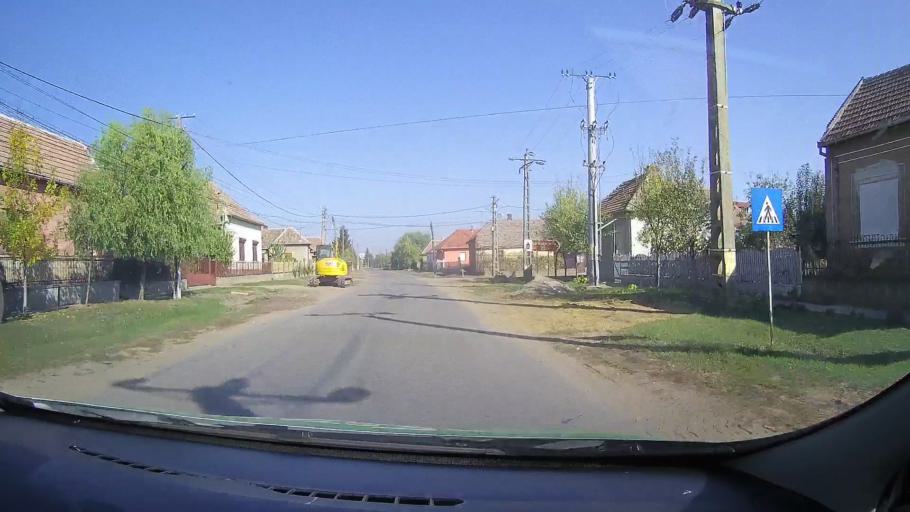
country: RO
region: Satu Mare
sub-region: Comuna Ciumesti
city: Ciumesti
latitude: 47.6635
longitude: 22.3365
